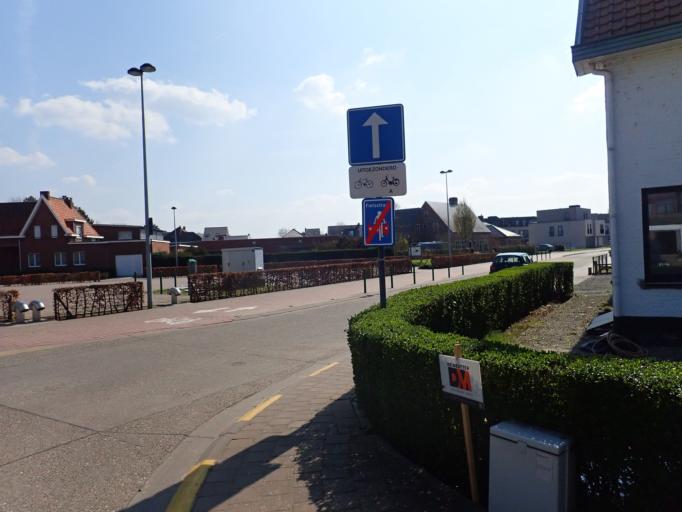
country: BE
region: Flanders
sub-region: Provincie Antwerpen
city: Heist-op-den-Berg
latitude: 51.0733
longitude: 4.7014
